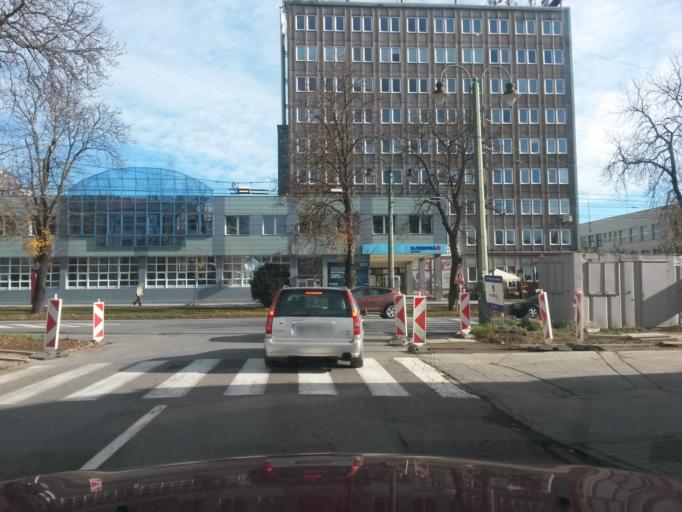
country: SK
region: Presovsky
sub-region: Okres Presov
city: Presov
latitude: 48.9907
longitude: 21.2457
